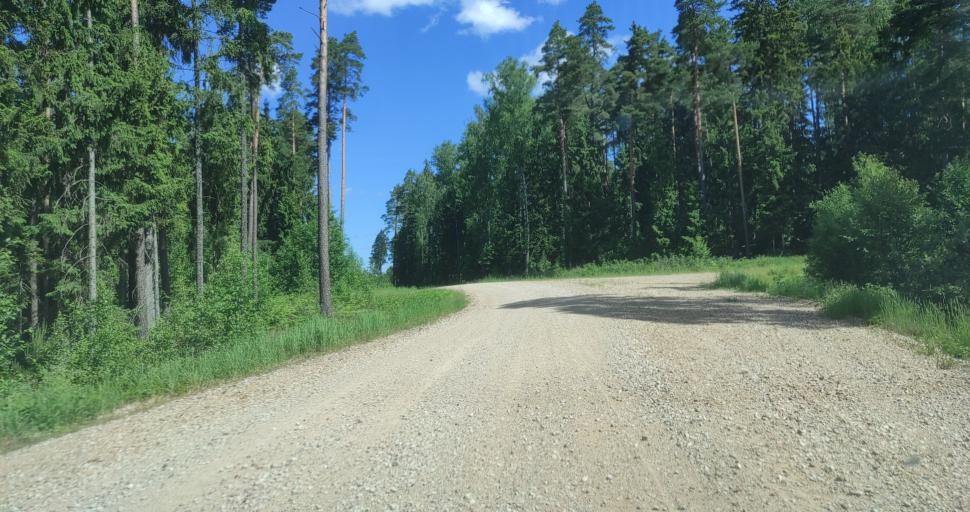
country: LV
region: Kuldigas Rajons
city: Kuldiga
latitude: 56.9408
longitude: 21.7903
